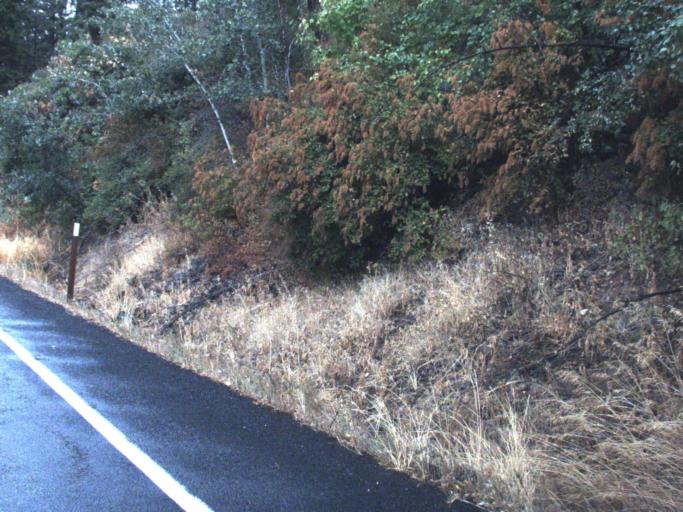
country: US
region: Washington
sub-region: Spokane County
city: Medical Lake
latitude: 47.7435
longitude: -117.8850
